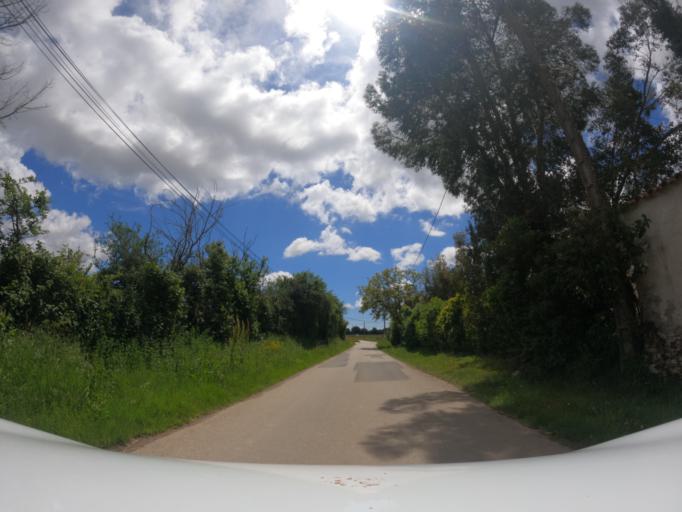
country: FR
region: Pays de la Loire
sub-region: Departement de la Vendee
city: Le Champ-Saint-Pere
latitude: 46.4859
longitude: -1.3581
